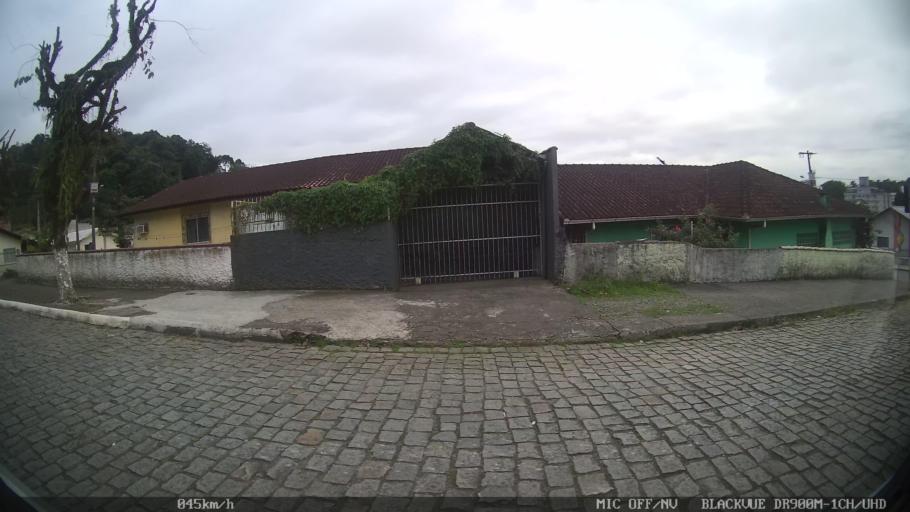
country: BR
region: Santa Catarina
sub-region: Joinville
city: Joinville
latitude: -26.2838
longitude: -48.8823
